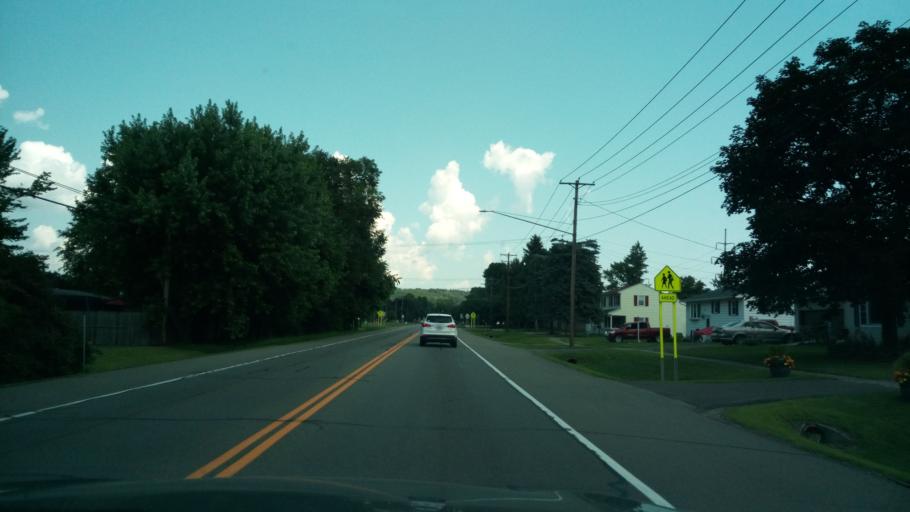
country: US
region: New York
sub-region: Chemung County
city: Horseheads
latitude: 42.1682
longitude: -76.8402
